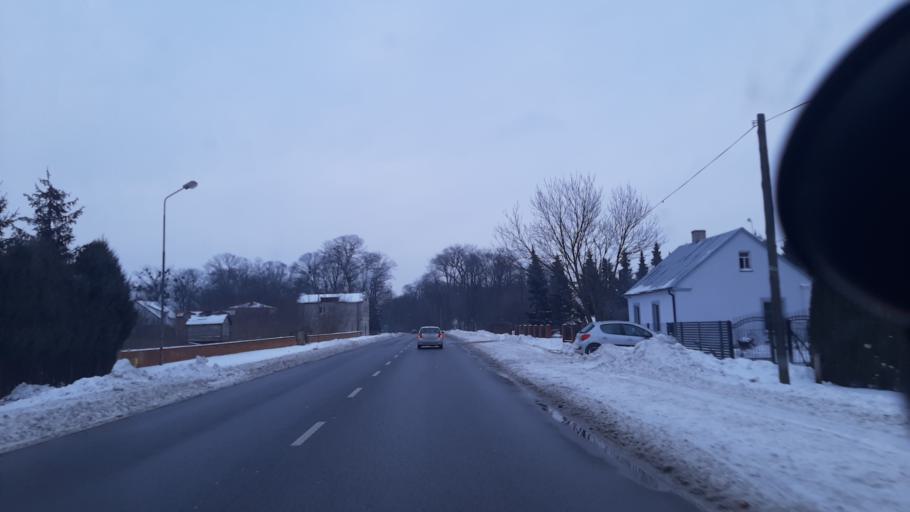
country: PL
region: Lublin Voivodeship
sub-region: Powiat lubelski
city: Garbow
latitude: 51.3558
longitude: 22.3269
